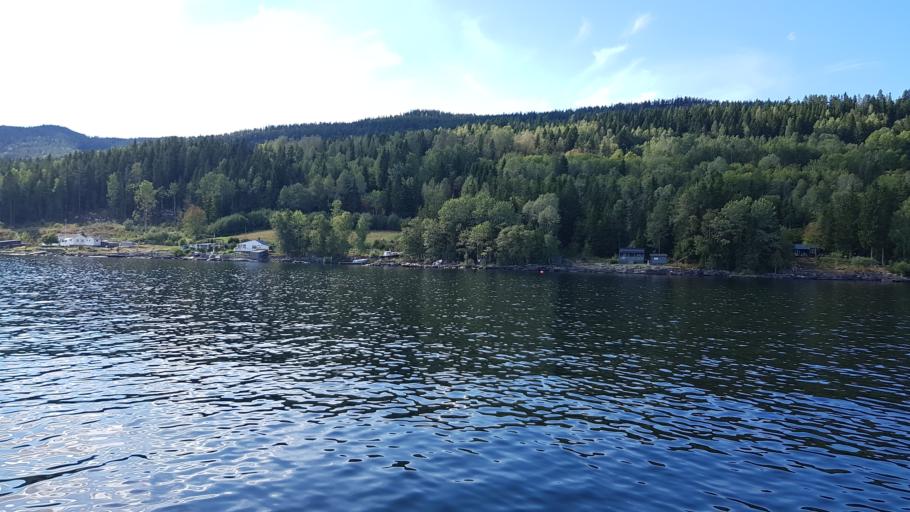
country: NO
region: Akershus
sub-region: Hurdal
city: Hurdal
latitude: 60.5455
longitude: 11.1983
